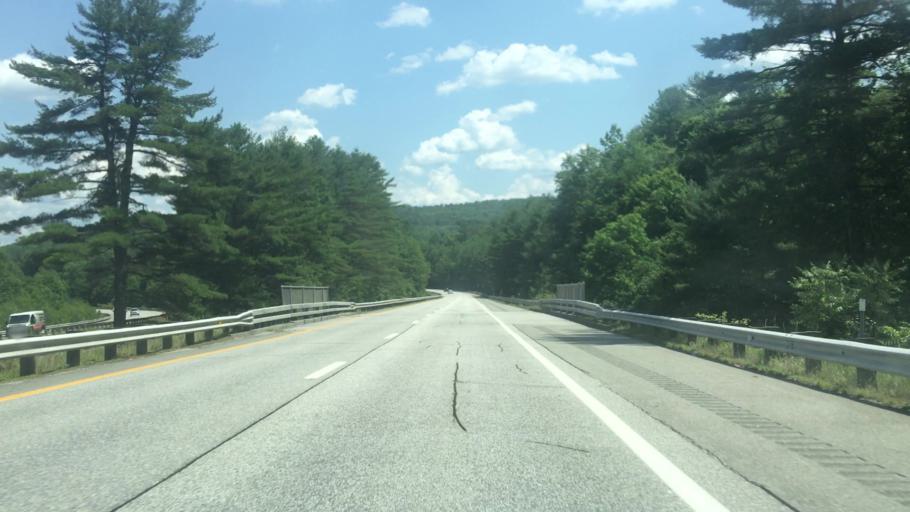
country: US
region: New Hampshire
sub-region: Merrimack County
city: Henniker
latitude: 43.2738
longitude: -71.8096
